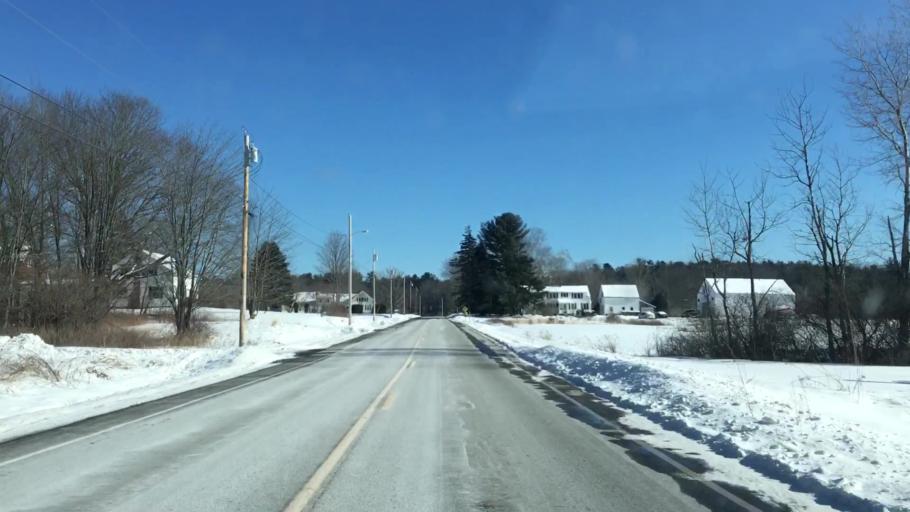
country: US
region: Maine
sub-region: Androscoggin County
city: Lisbon
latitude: 44.0298
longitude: -70.0862
